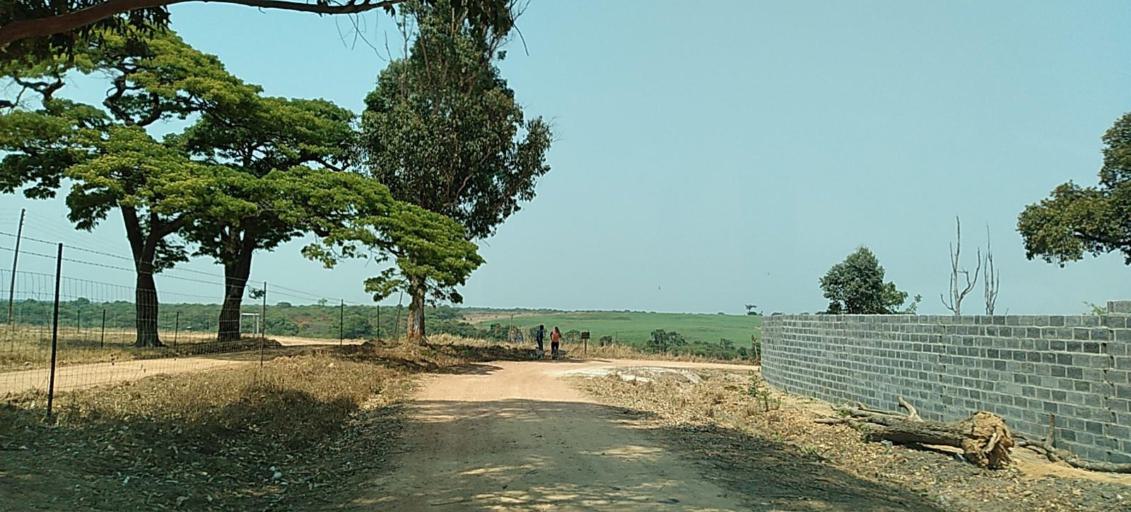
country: ZM
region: Copperbelt
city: Chambishi
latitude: -12.6305
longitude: 27.9439
